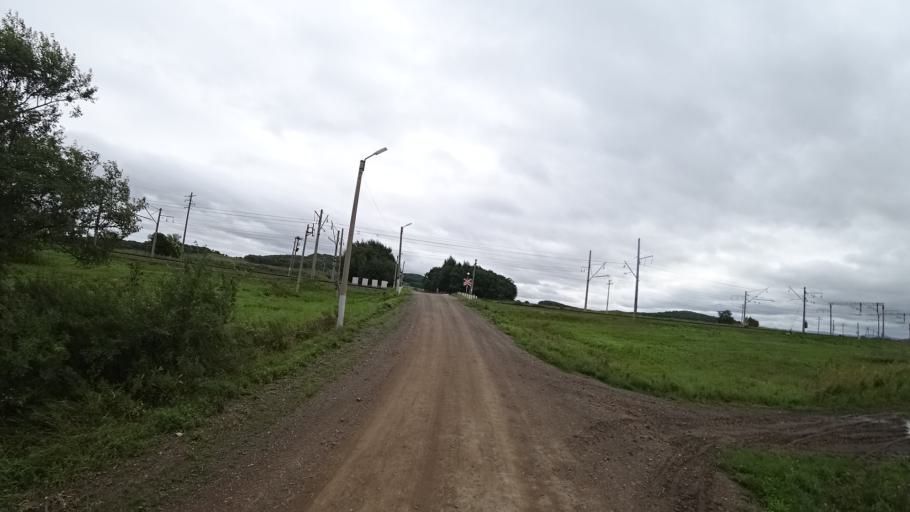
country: RU
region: Primorskiy
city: Chernigovka
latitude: 44.4803
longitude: 132.5753
